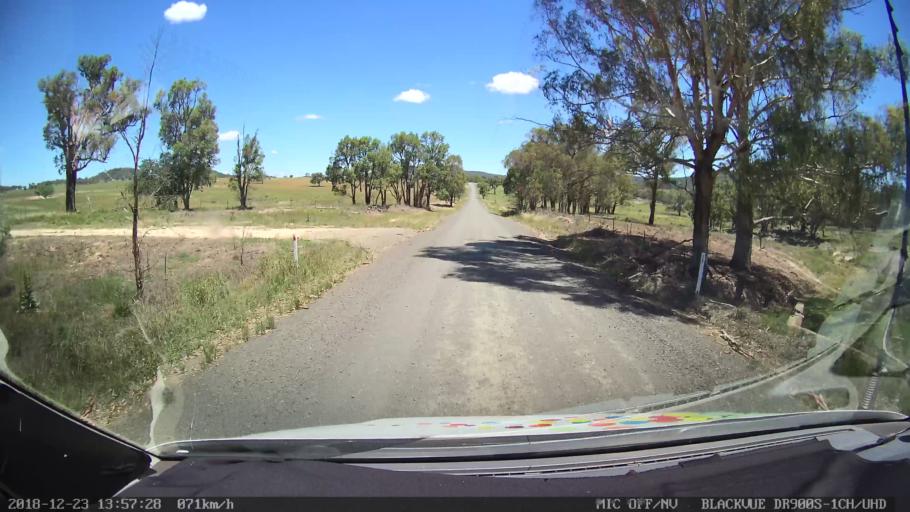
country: AU
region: New South Wales
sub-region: Tamworth Municipality
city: Manilla
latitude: -30.5882
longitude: 151.0938
